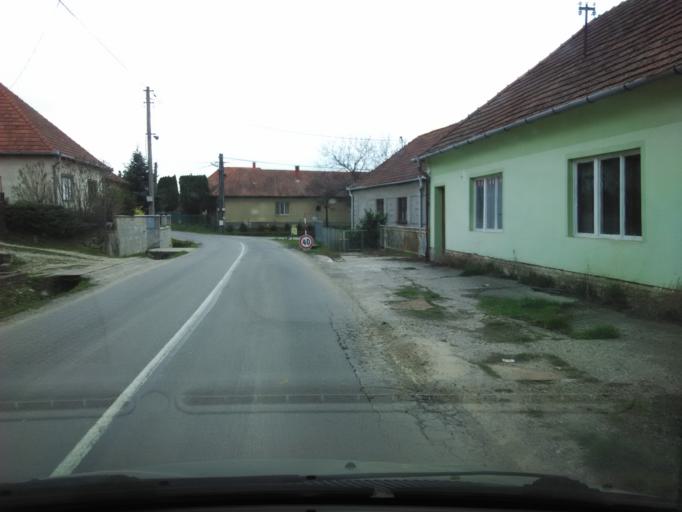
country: SK
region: Nitriansky
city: Zlate Moravce
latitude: 48.4115
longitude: 18.3049
